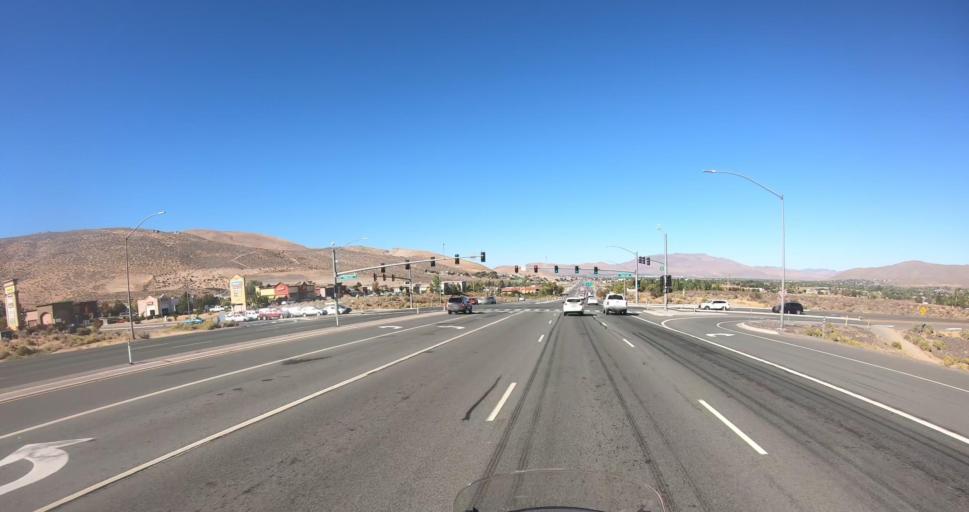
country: US
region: Nevada
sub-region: Douglas County
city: Indian Hills
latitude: 39.1096
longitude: -119.7730
